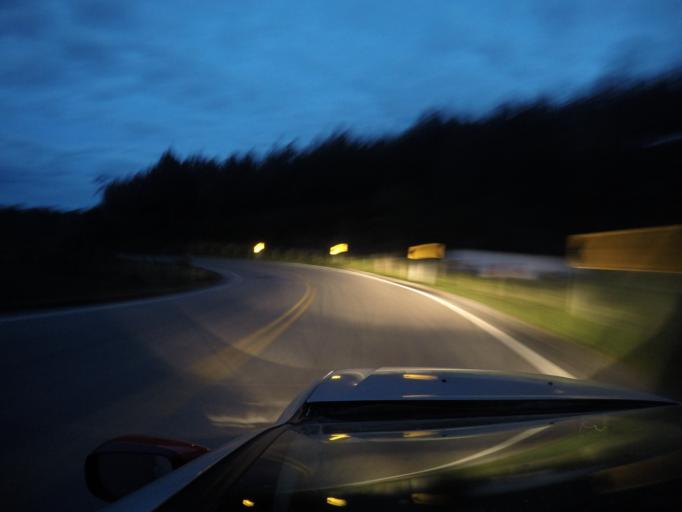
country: CO
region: Tolima
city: Fresno
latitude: 5.1594
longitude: -75.0890
